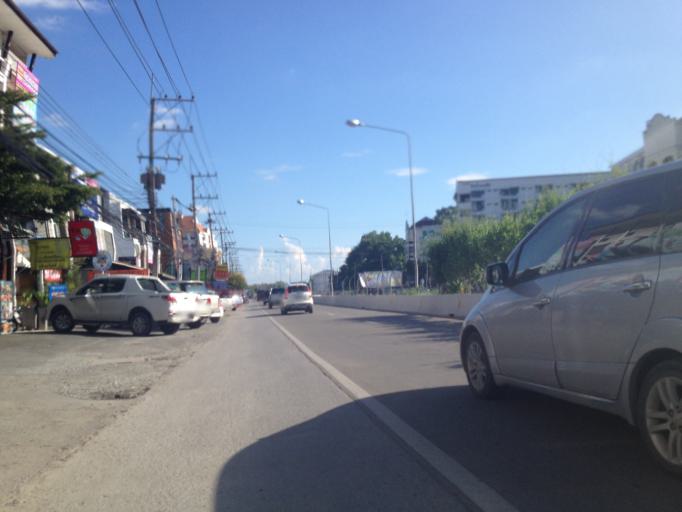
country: TH
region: Chiang Mai
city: Chiang Mai
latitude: 18.8012
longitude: 98.9603
